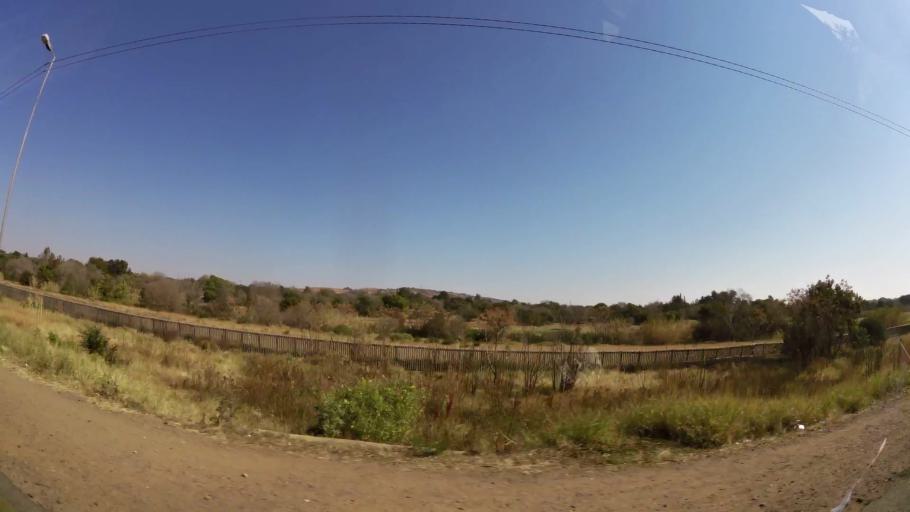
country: ZA
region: Gauteng
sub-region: City of Tshwane Metropolitan Municipality
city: Pretoria
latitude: -25.6896
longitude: 28.2935
